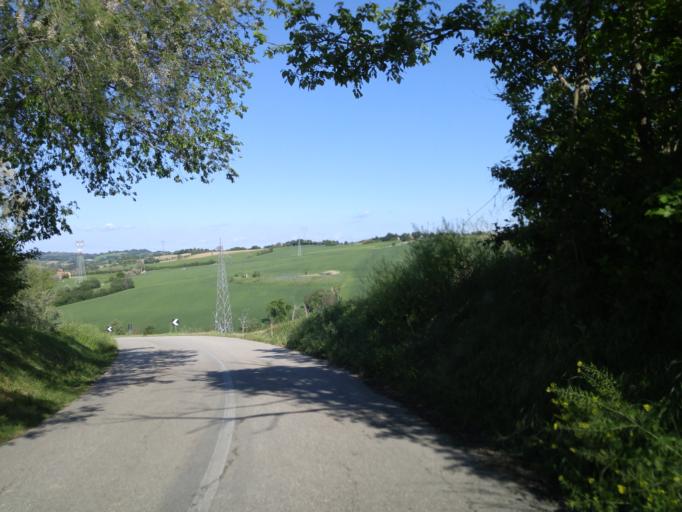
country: IT
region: The Marches
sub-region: Provincia di Pesaro e Urbino
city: Mombaroccio
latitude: 43.8271
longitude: 12.8582
